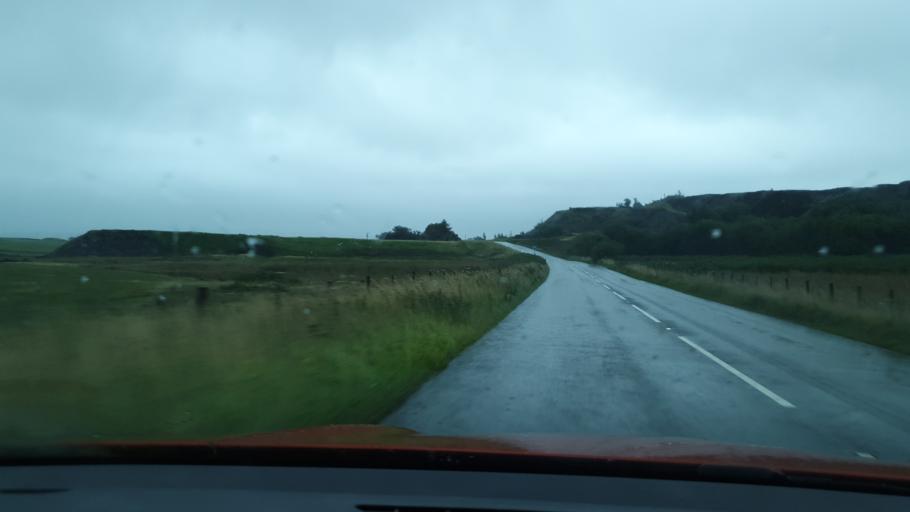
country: GB
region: England
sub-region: Cumbria
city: Ulverston
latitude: 54.2538
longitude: -3.1304
